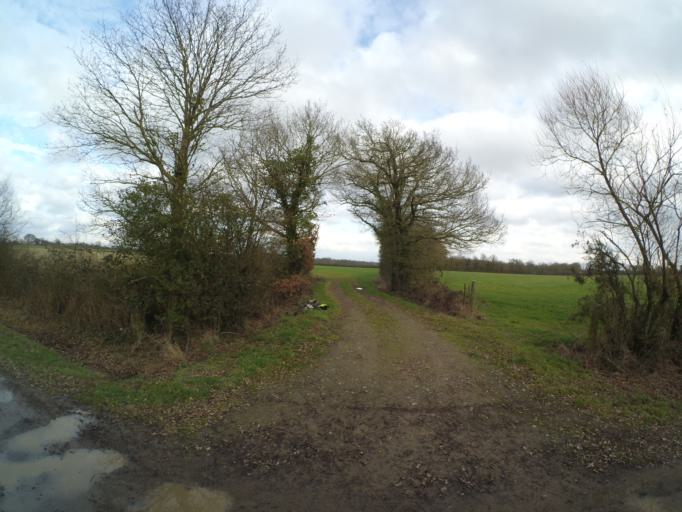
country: FR
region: Pays de la Loire
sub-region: Departement de la Loire-Atlantique
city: Saint-Hilaire-de-Clisson
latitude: 47.0582
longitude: -1.2873
